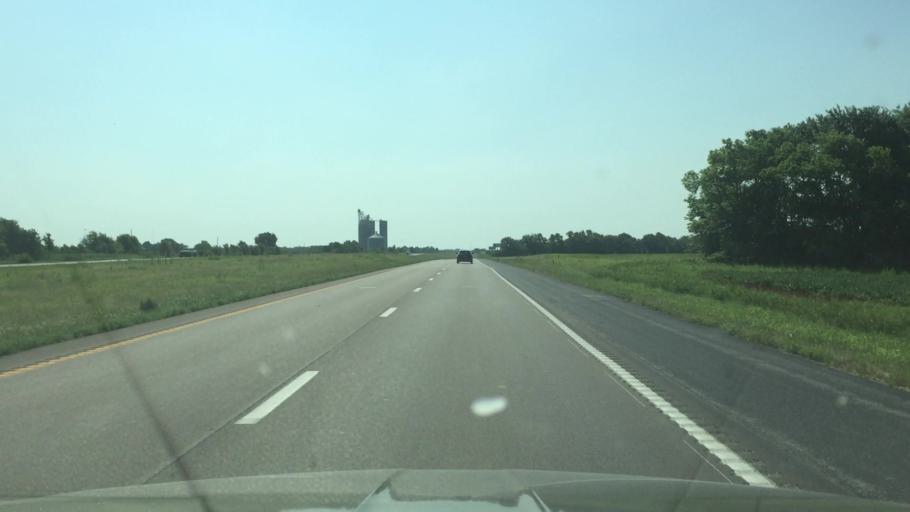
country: US
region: Missouri
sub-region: Pettis County
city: La Monte
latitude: 38.7550
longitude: -93.3603
